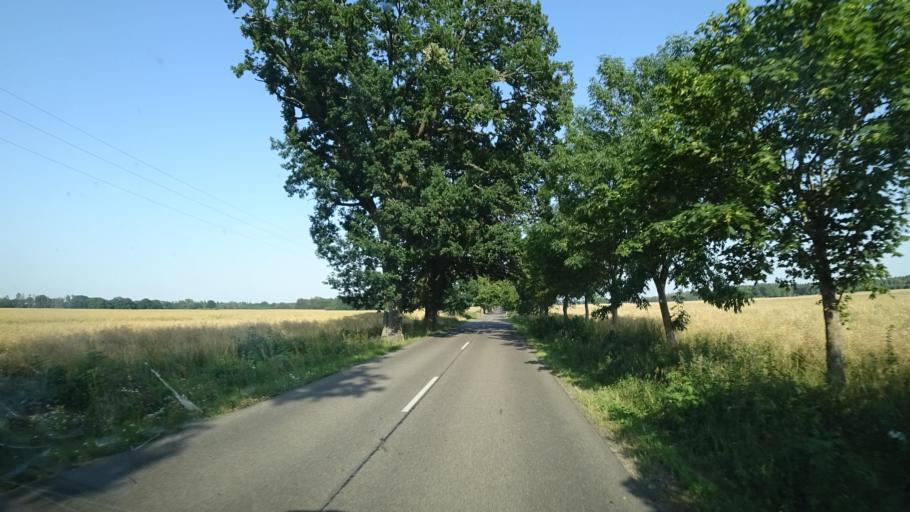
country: PL
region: Pomeranian Voivodeship
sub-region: Powiat czluchowski
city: Przechlewo
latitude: 53.8042
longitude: 17.2914
